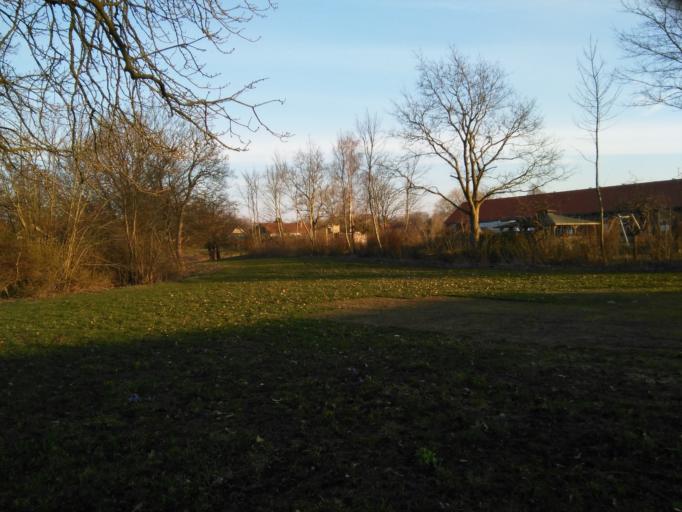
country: DK
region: Central Jutland
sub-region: Arhus Kommune
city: Beder
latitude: 56.0631
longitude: 10.2073
